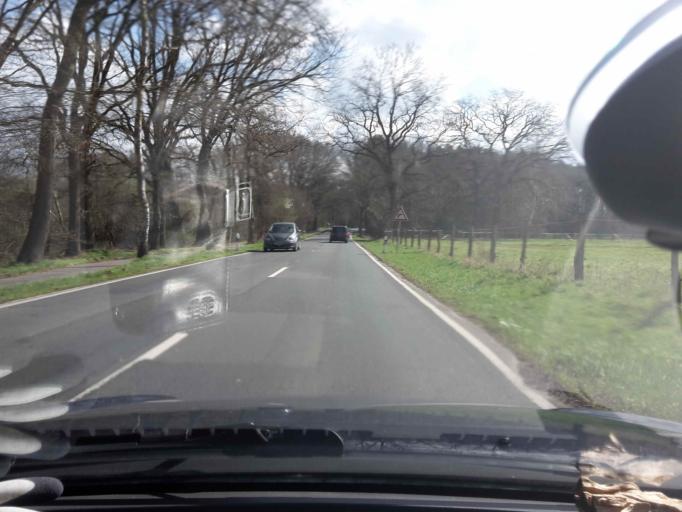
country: DE
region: Lower Saxony
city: Asendorf
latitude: 53.2884
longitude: 9.9963
